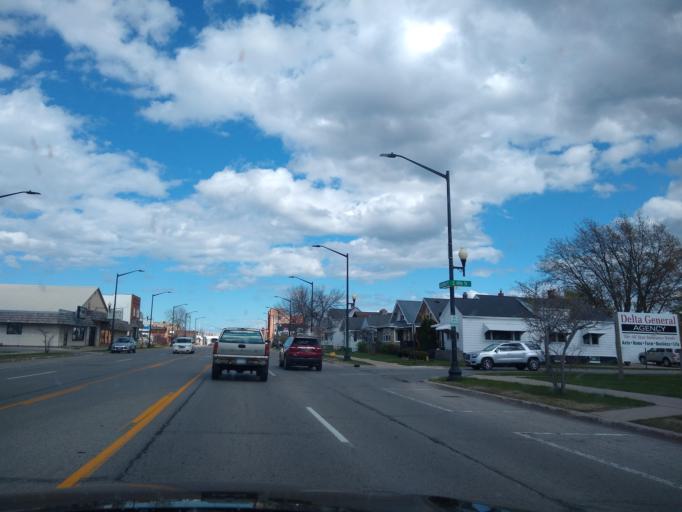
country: US
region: Michigan
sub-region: Delta County
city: Escanaba
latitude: 45.7457
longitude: -87.0745
